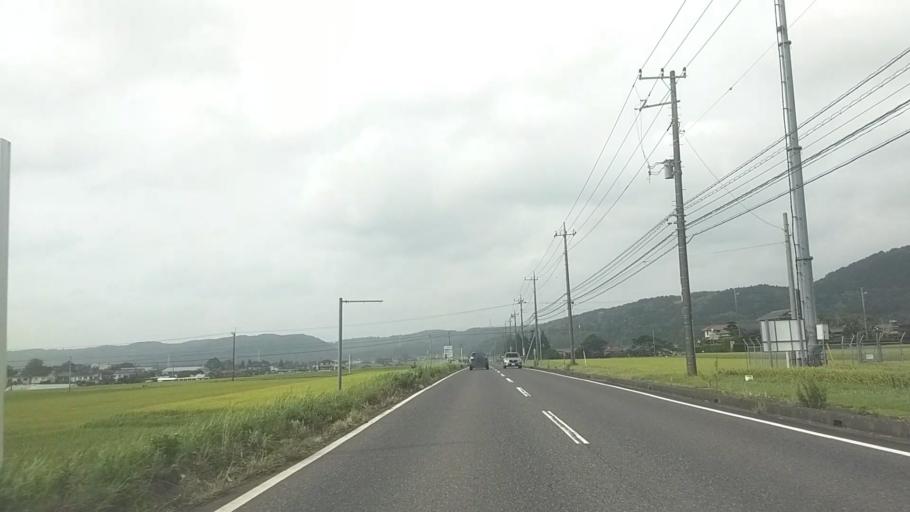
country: JP
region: Chiba
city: Kimitsu
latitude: 35.2854
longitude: 139.9902
